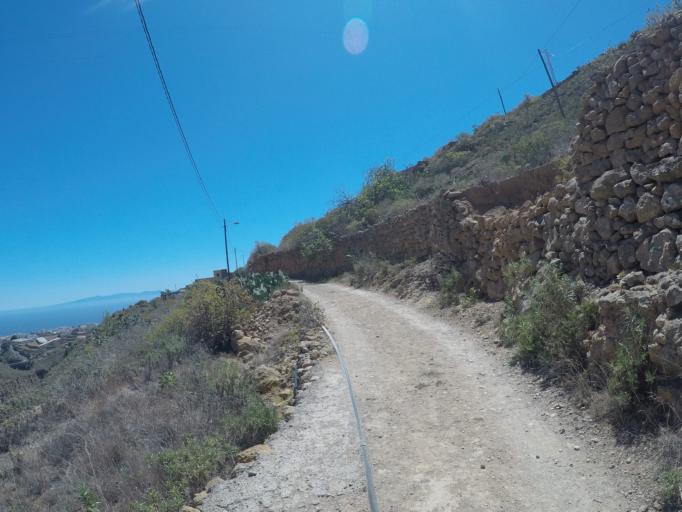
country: ES
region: Canary Islands
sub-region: Provincia de Santa Cruz de Tenerife
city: Lomo de Arico
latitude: 28.1835
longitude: -16.4888
